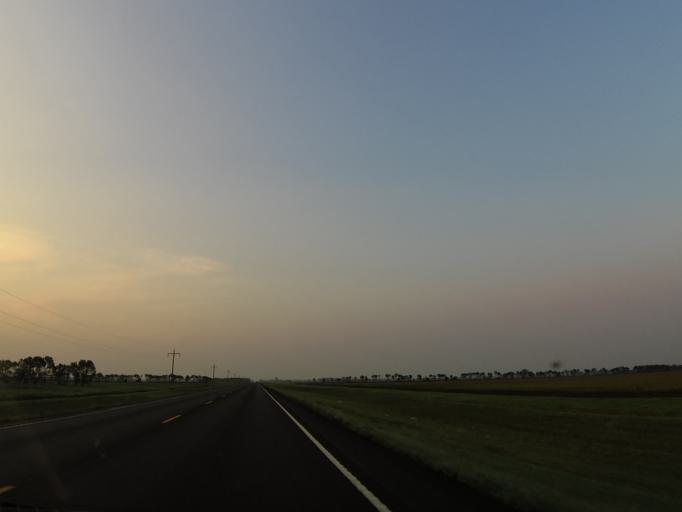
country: US
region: North Dakota
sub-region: Walsh County
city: Park River
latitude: 48.2982
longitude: -97.6227
